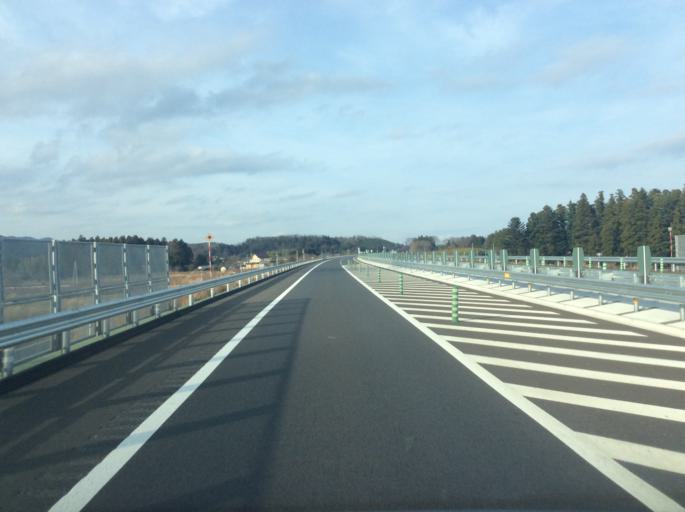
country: JP
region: Fukushima
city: Namie
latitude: 37.4028
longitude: 140.9635
